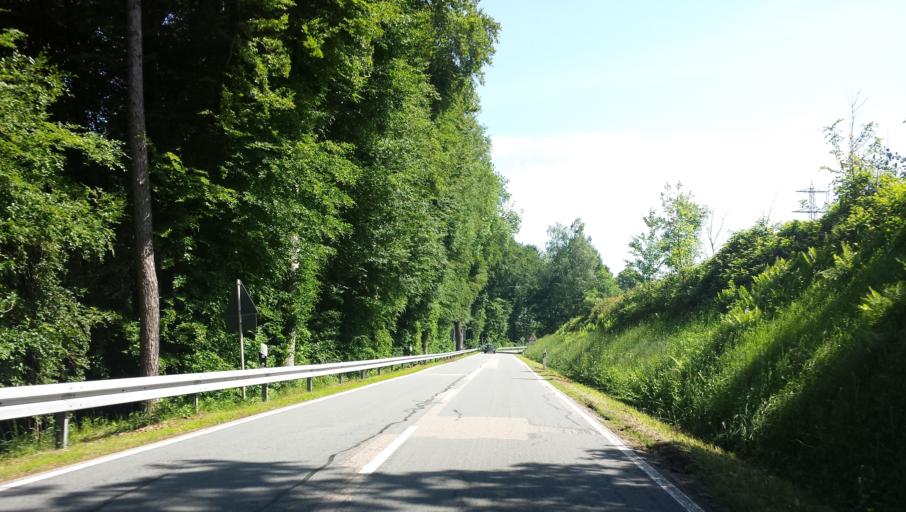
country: DE
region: Hesse
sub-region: Regierungsbezirk Darmstadt
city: Beerfelden
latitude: 49.5494
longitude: 8.9306
